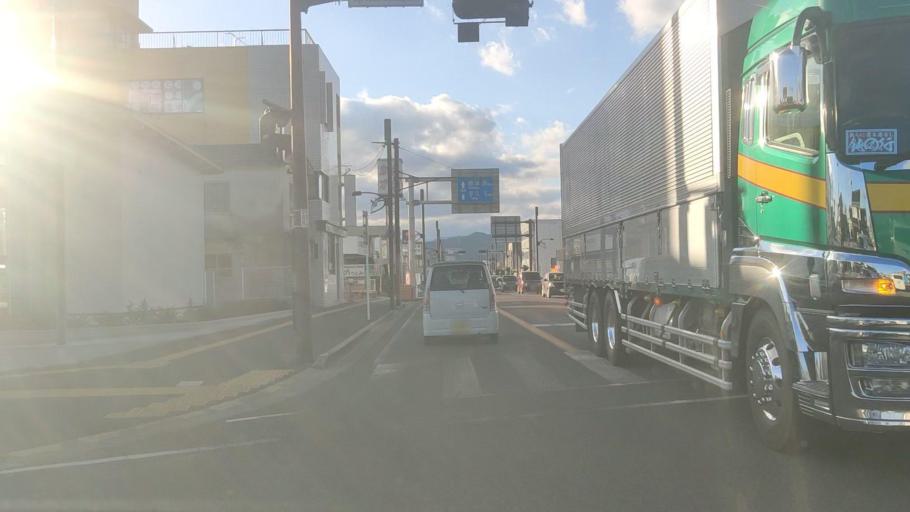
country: JP
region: Saga Prefecture
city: Saga-shi
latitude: 33.2936
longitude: 130.1999
